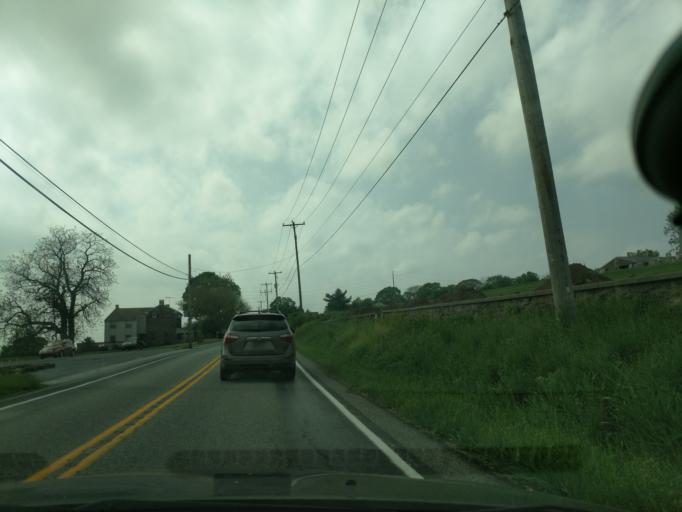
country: US
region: Pennsylvania
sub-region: Chester County
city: Spring City
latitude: 40.1550
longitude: -75.5676
